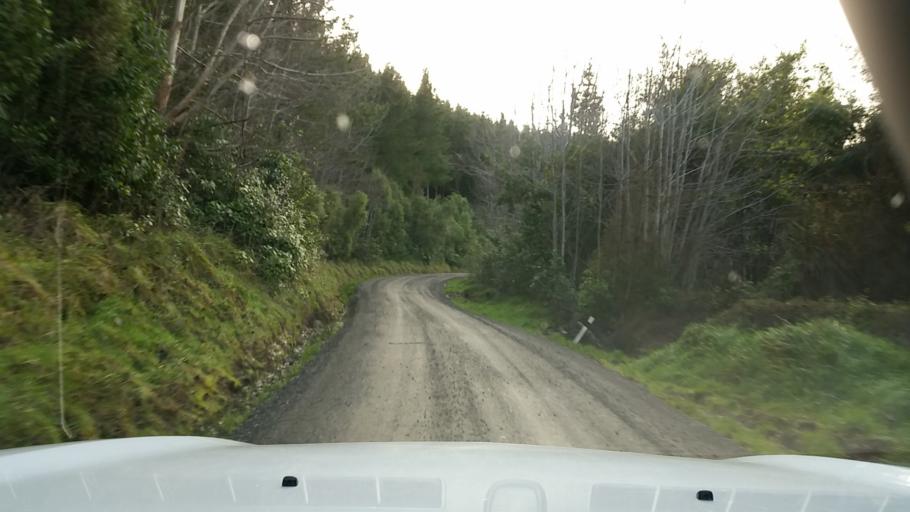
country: NZ
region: Wellington
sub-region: Masterton District
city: Masterton
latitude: -41.1859
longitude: 175.9578
